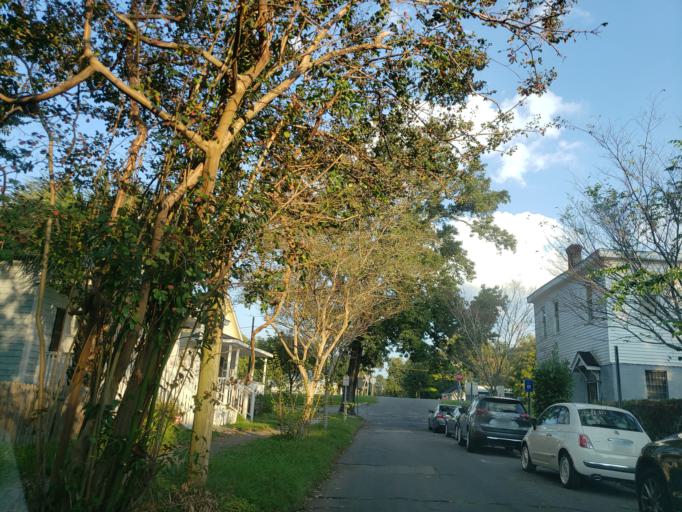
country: US
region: Georgia
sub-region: Chatham County
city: Savannah
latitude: 32.0587
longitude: -81.0926
